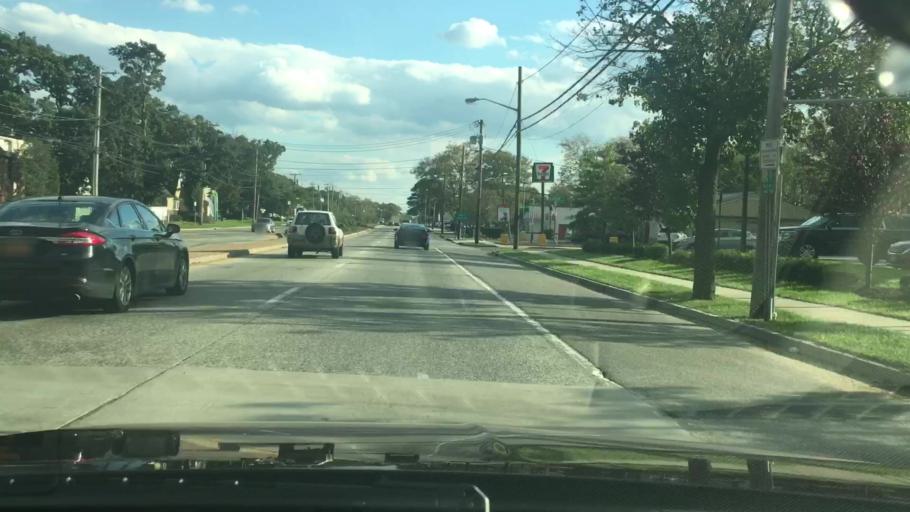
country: US
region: New York
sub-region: Suffolk County
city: Deer Park
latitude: 40.7753
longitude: -73.3353
